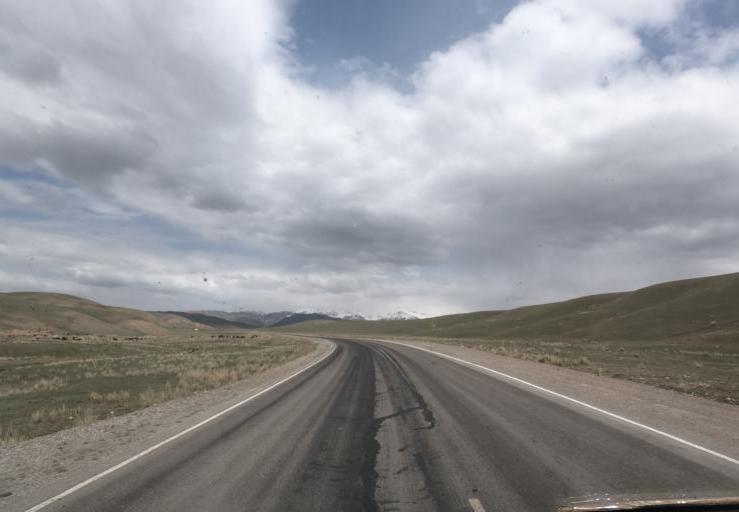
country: KG
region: Naryn
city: Naryn
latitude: 41.2751
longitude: 75.9834
